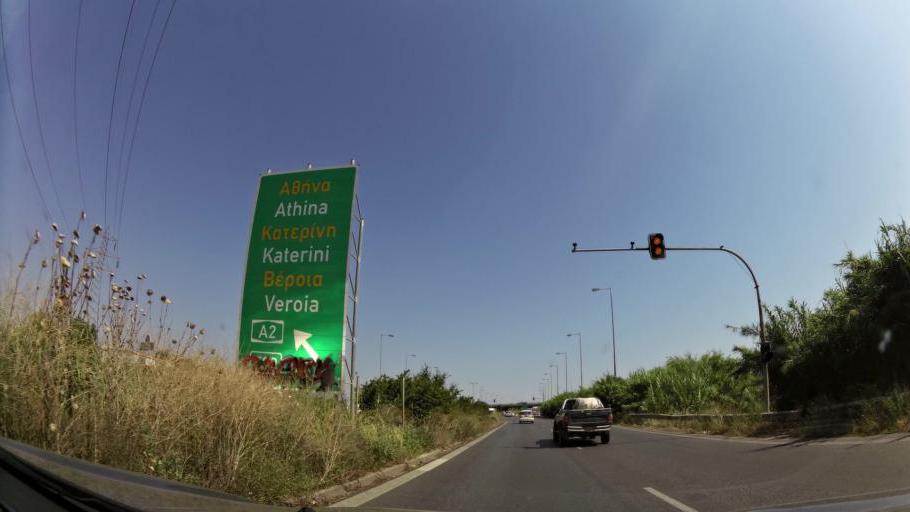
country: GR
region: Central Macedonia
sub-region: Nomos Thessalonikis
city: Nea Magnisia
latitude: 40.6963
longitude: 22.8441
